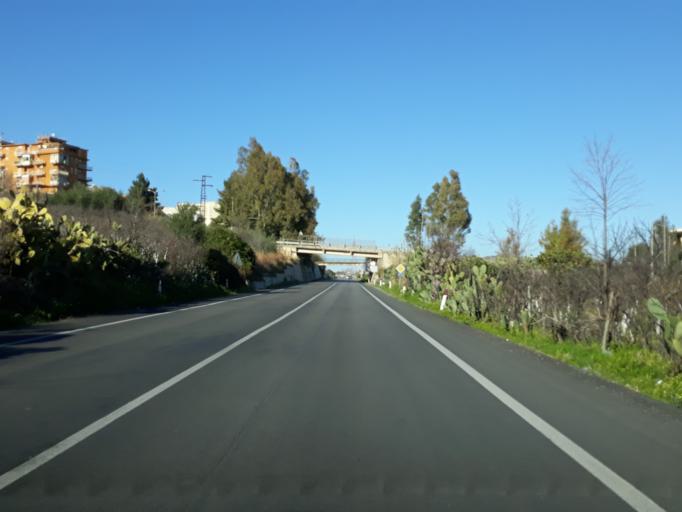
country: IT
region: Sicily
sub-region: Palermo
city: Misilmeri
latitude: 38.0353
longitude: 13.4590
